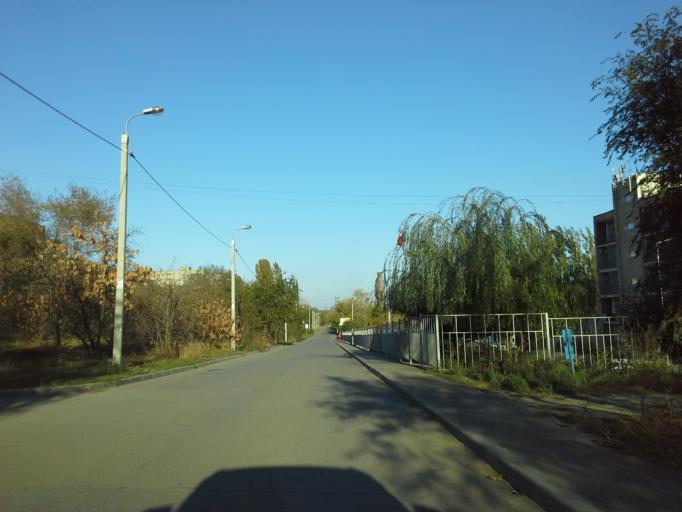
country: RU
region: Volgograd
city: Vodstroy
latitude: 48.8188
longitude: 44.6382
